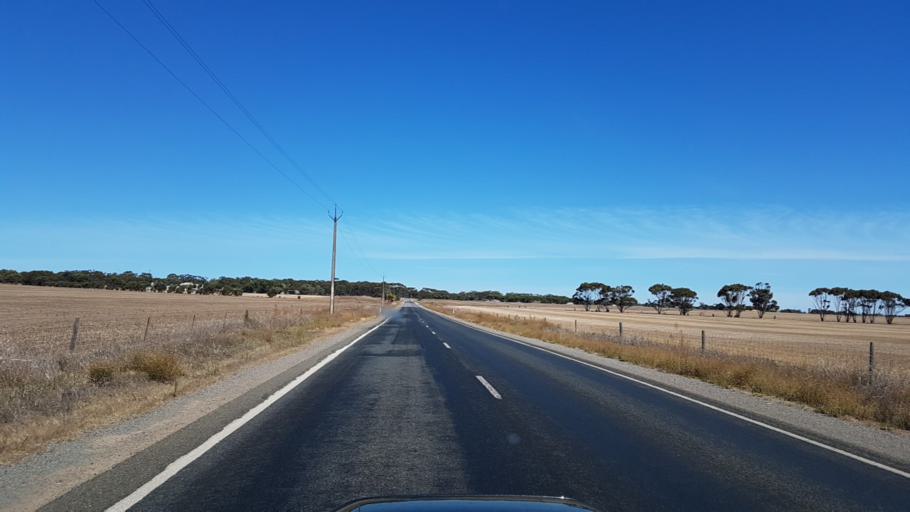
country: AU
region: South Australia
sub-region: Yorke Peninsula
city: Maitland
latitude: -34.3597
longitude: 137.6662
